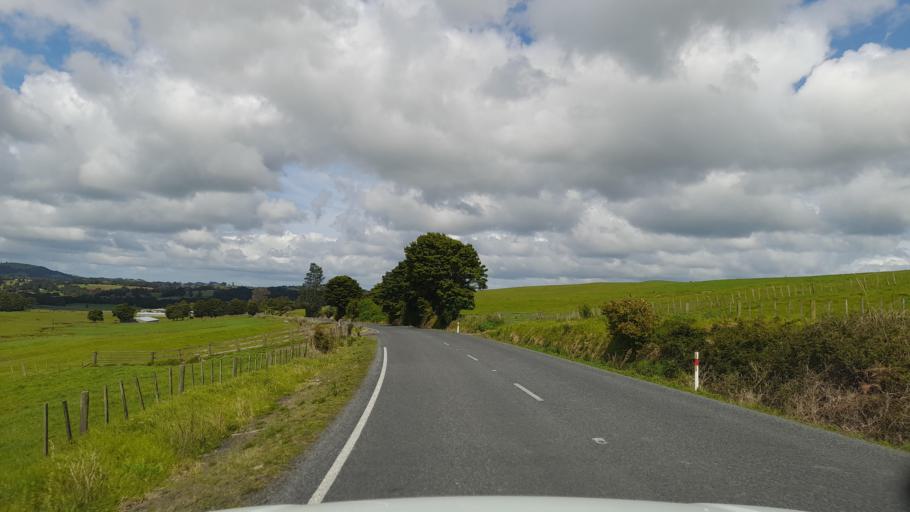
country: NZ
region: Northland
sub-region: Whangarei
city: Maungatapere
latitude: -35.6529
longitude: 174.1256
